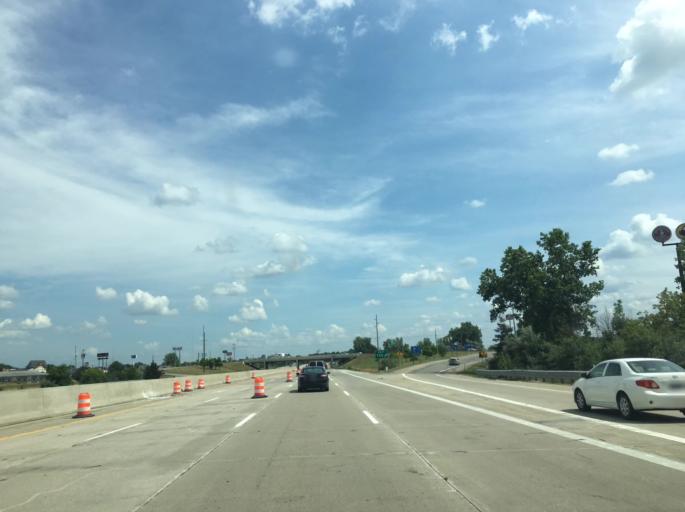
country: US
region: Michigan
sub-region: Saginaw County
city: Birch Run
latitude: 43.2529
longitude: -83.7781
